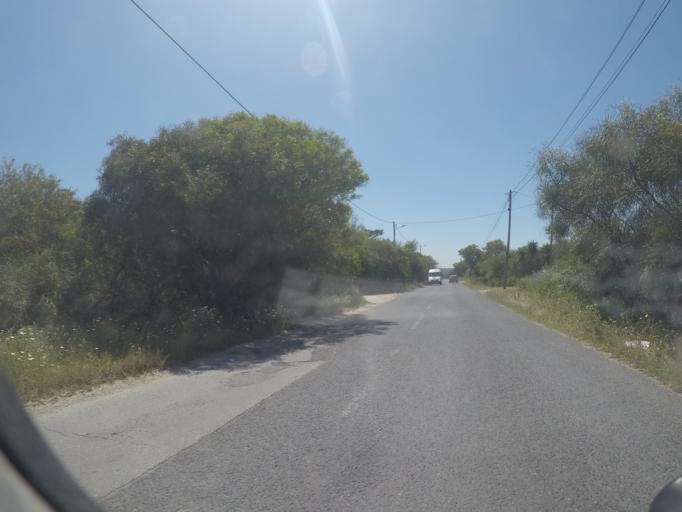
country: PT
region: Setubal
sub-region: Almada
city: Charneca
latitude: 38.6202
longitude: -9.2138
